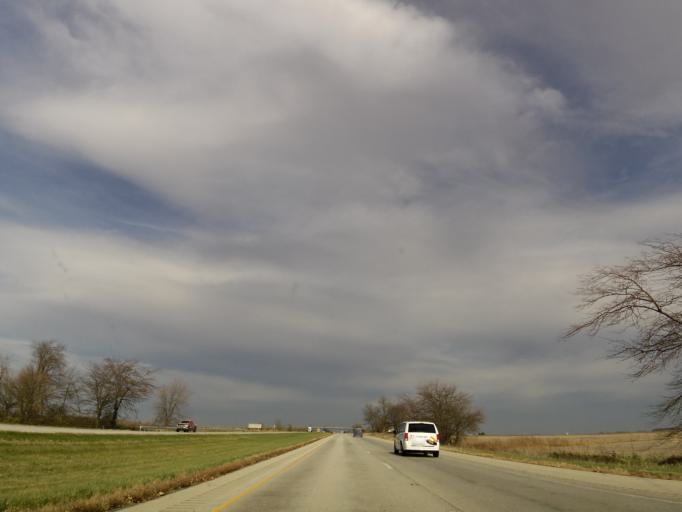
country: US
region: Illinois
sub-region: Knox County
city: Galesburg
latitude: 41.0177
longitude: -90.3346
